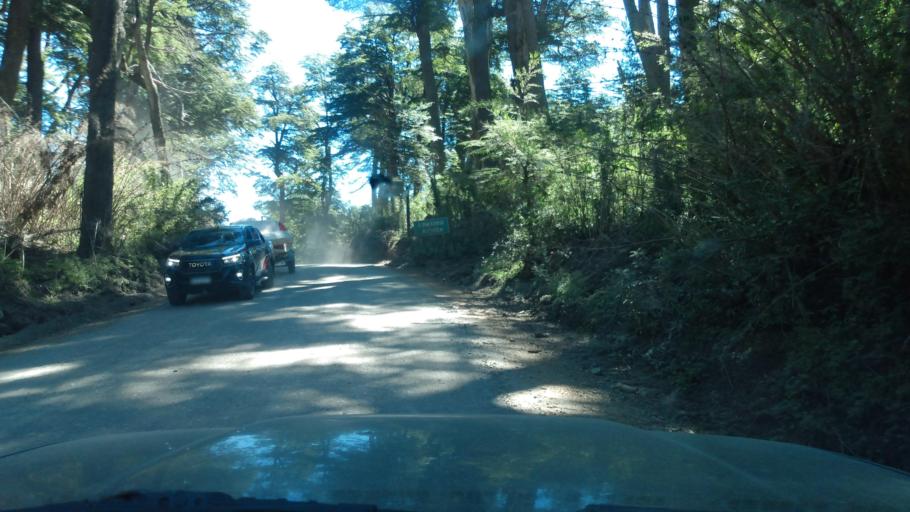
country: AR
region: Neuquen
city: Villa La Angostura
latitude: -40.6048
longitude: -71.6412
